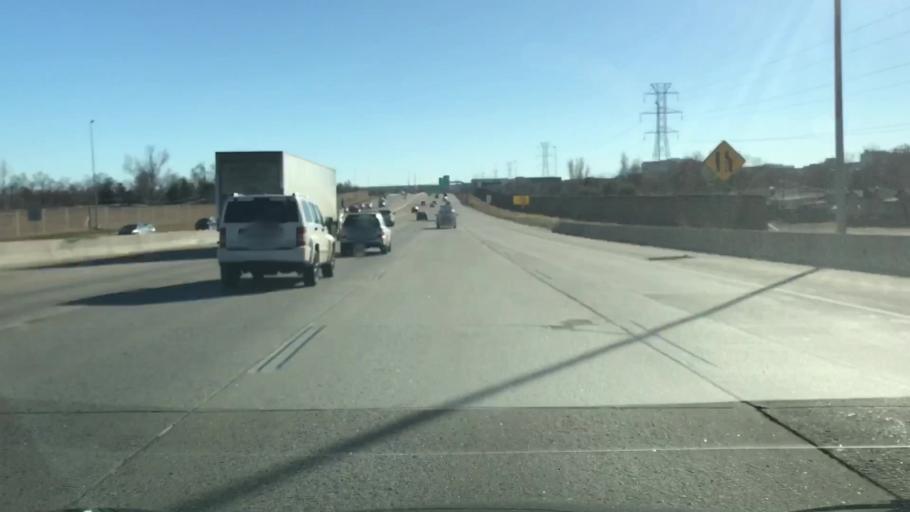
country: US
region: Colorado
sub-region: Adams County
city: Aurora
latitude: 39.7625
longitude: -104.8278
